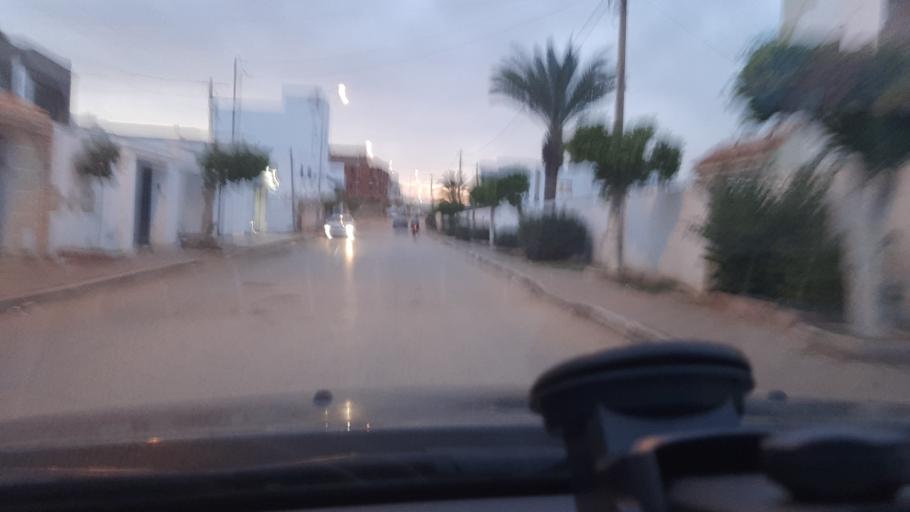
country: TN
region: Safaqis
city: Sfax
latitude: 34.7653
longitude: 10.6985
